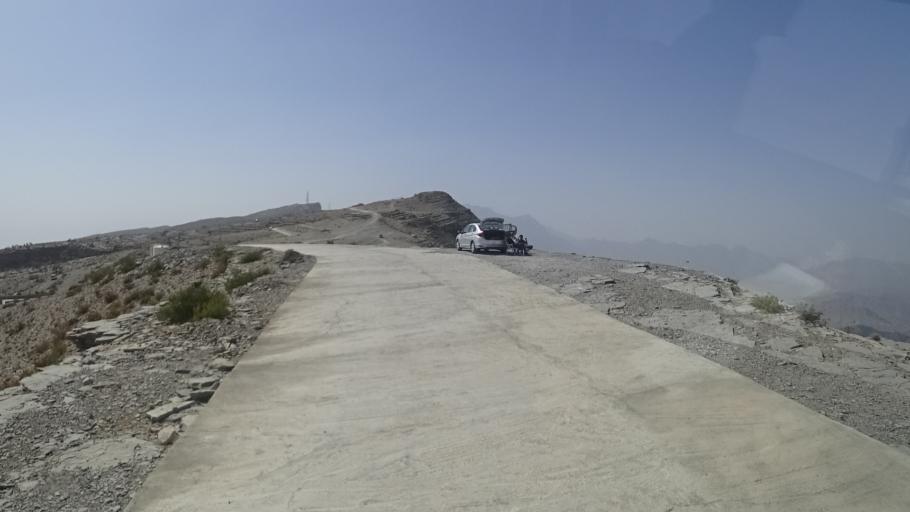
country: OM
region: Al Batinah
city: Bayt al `Awabi
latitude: 23.1677
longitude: 57.4143
